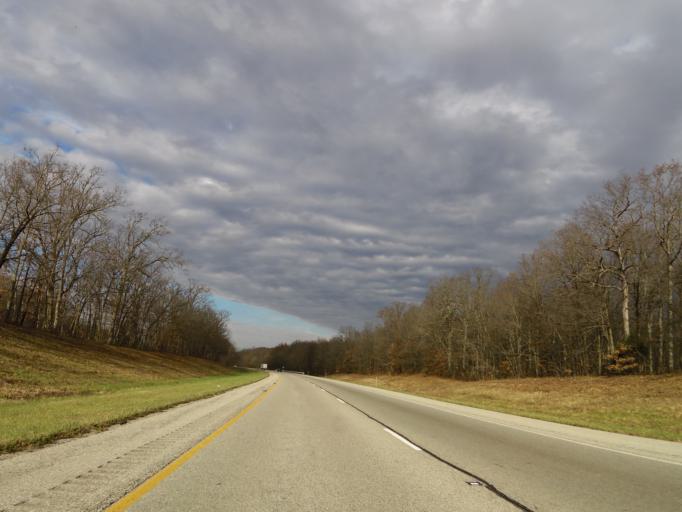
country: US
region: Illinois
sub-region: Washington County
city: Nashville
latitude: 38.3975
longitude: -89.3905
